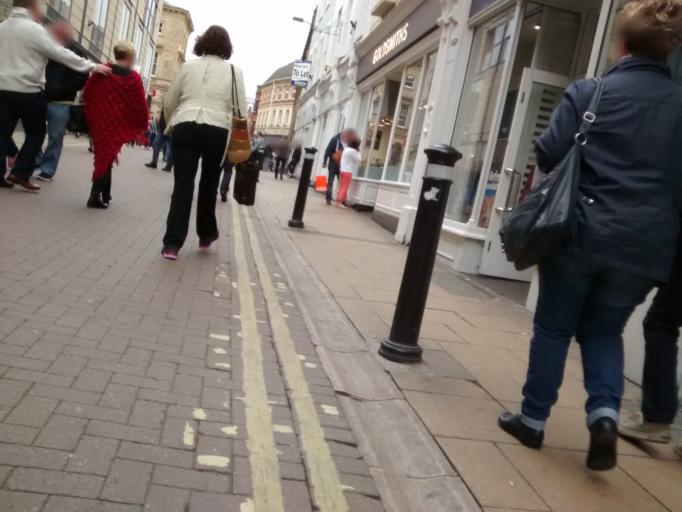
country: GB
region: England
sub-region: City of York
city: York
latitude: 53.9583
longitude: -1.0828
